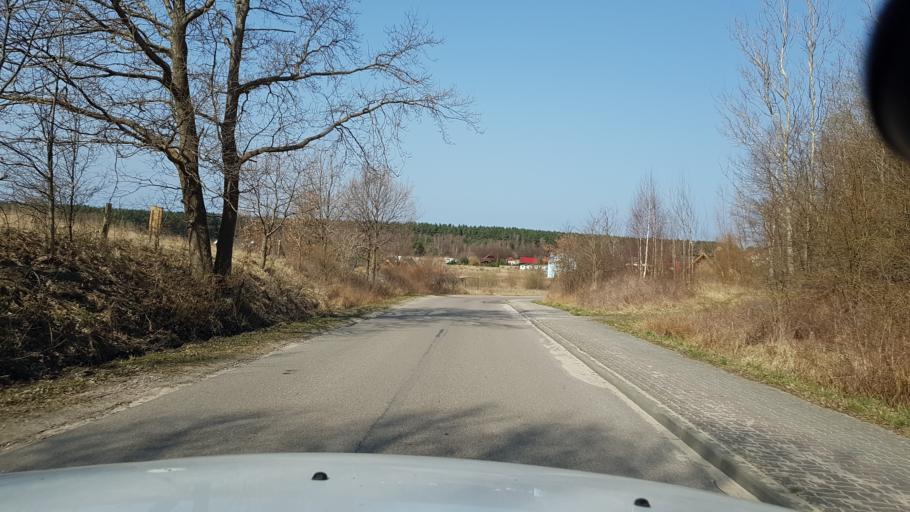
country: PL
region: West Pomeranian Voivodeship
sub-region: Powiat slawienski
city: Darlowo
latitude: 54.5145
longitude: 16.5168
